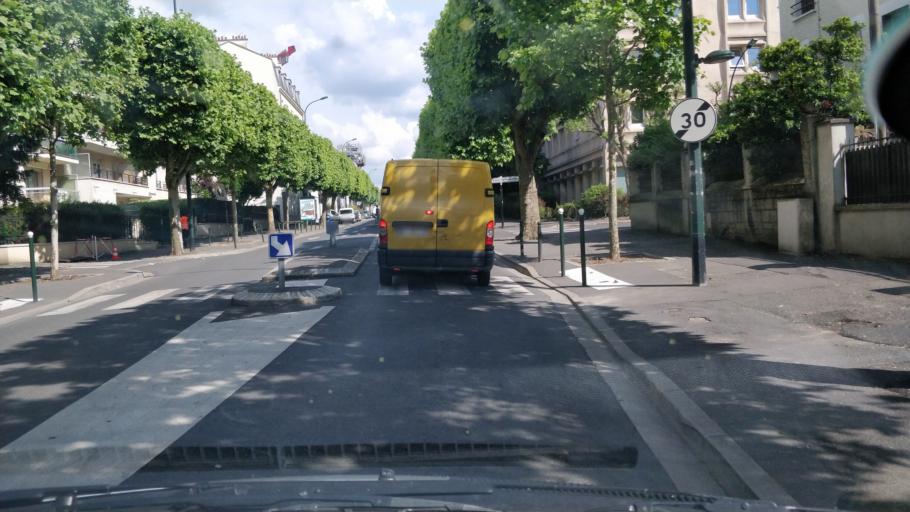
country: FR
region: Ile-de-France
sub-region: Departement de Seine-Saint-Denis
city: Le Raincy
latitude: 48.9004
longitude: 2.5146
